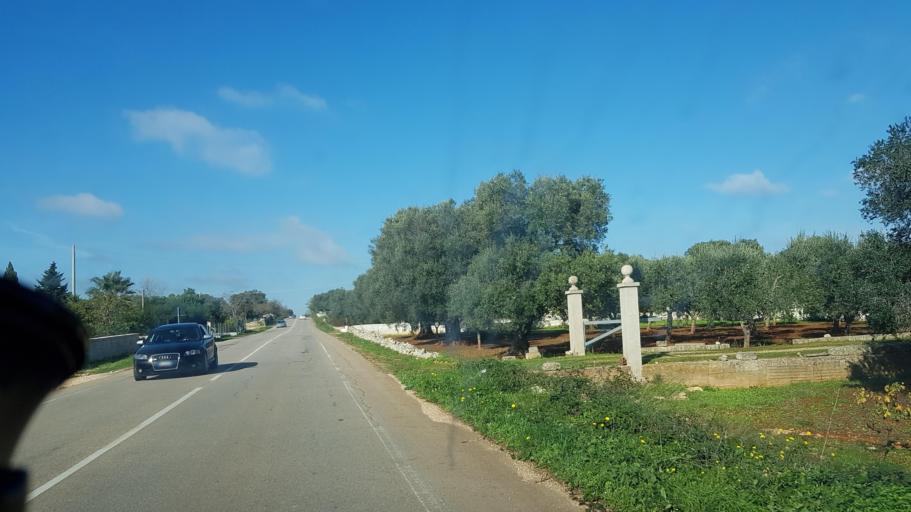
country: IT
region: Apulia
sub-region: Provincia di Brindisi
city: Carovigno
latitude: 40.6845
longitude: 17.6799
